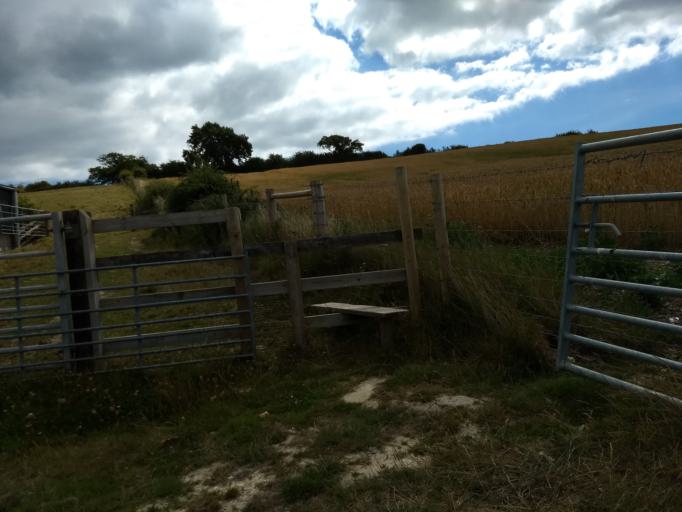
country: GB
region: England
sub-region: Isle of Wight
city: Ryde
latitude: 50.7083
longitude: -1.1884
